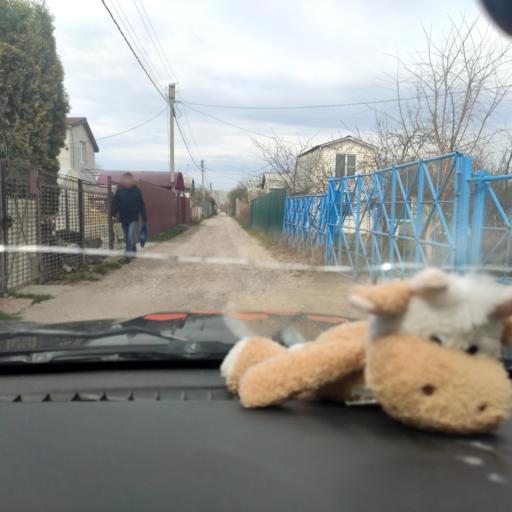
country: RU
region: Samara
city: Tol'yatti
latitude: 53.5998
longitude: 49.2405
